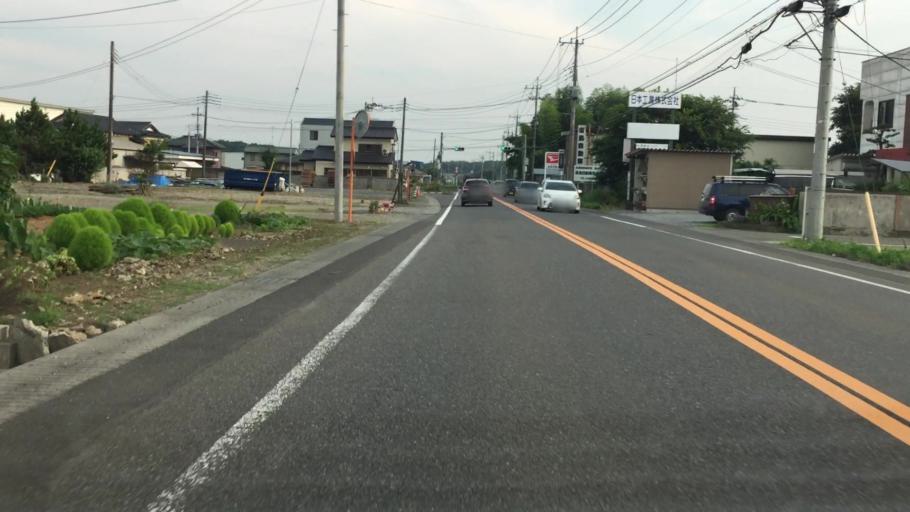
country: JP
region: Tochigi
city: Fujioka
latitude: 36.3073
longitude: 139.6715
